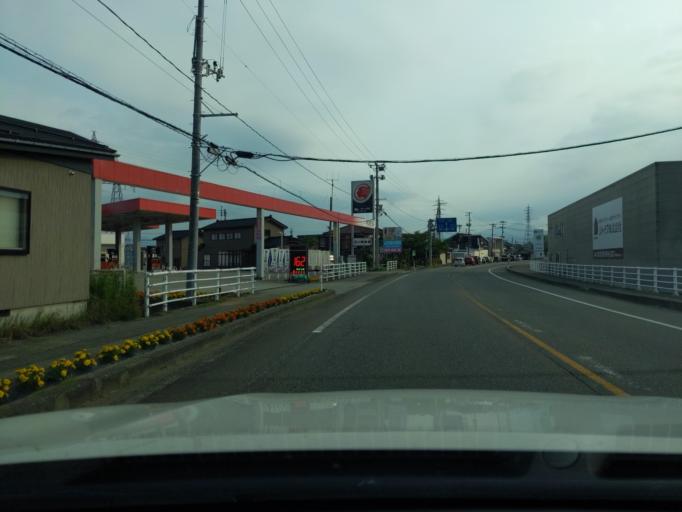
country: JP
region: Niigata
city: Kashiwazaki
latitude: 37.3939
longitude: 138.6021
